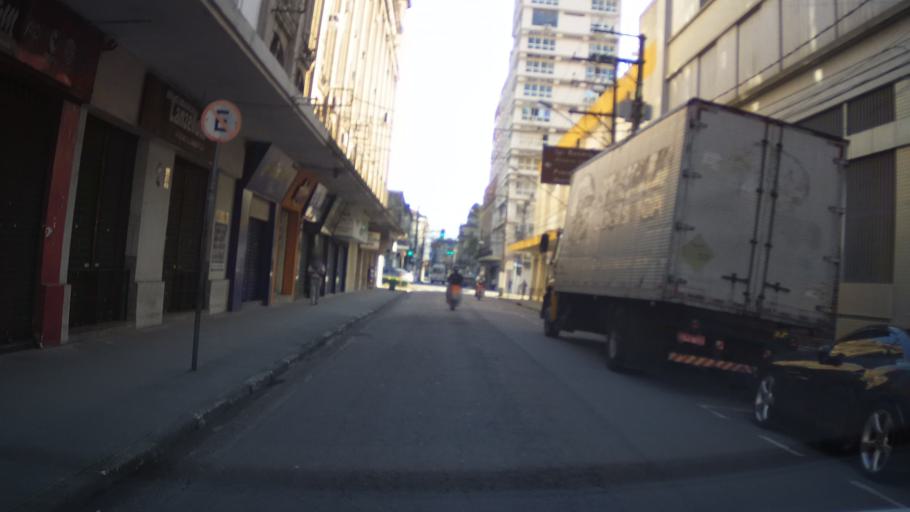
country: BR
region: Sao Paulo
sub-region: Santos
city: Santos
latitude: -23.9354
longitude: -46.3288
